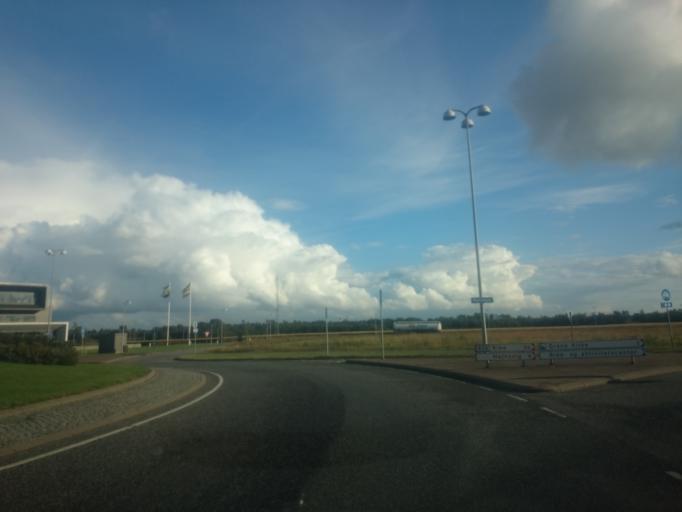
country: DK
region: South Denmark
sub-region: Billund Kommune
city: Billund
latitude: 55.7366
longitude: 9.0942
